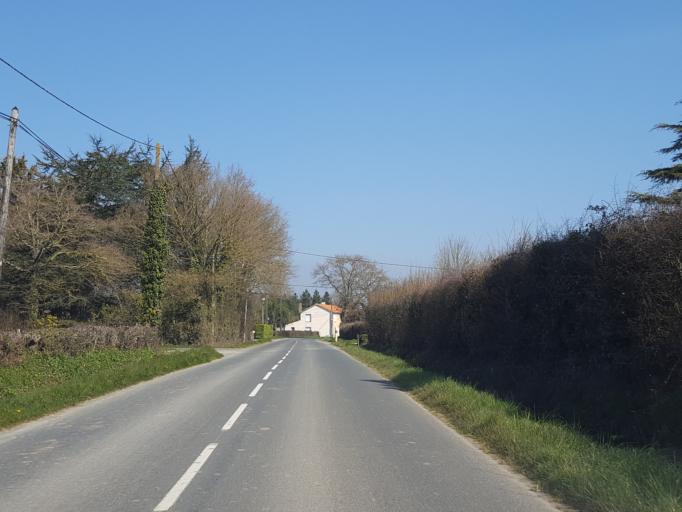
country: FR
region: Pays de la Loire
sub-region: Departement de la Vendee
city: La Chaize-le-Vicomte
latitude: 46.6594
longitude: -1.2986
